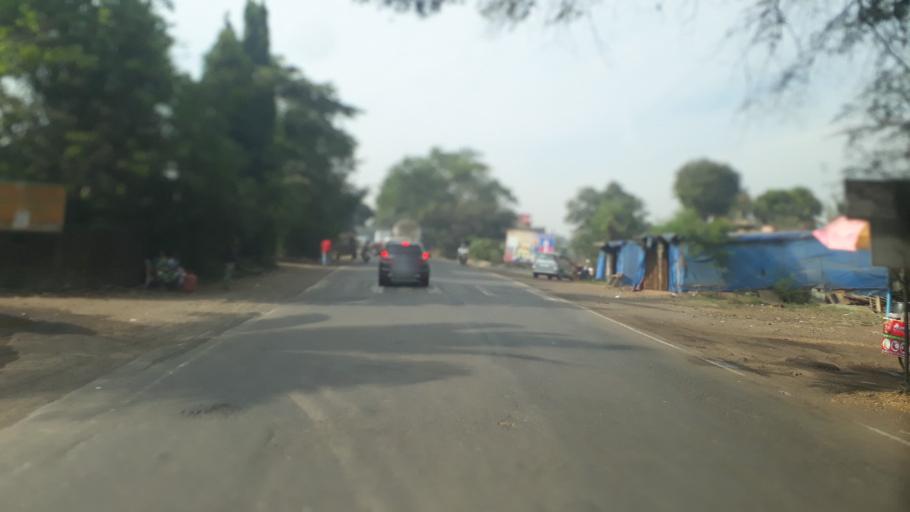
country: IN
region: Maharashtra
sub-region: Raigarh
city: Pen
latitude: 18.7175
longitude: 73.0610
